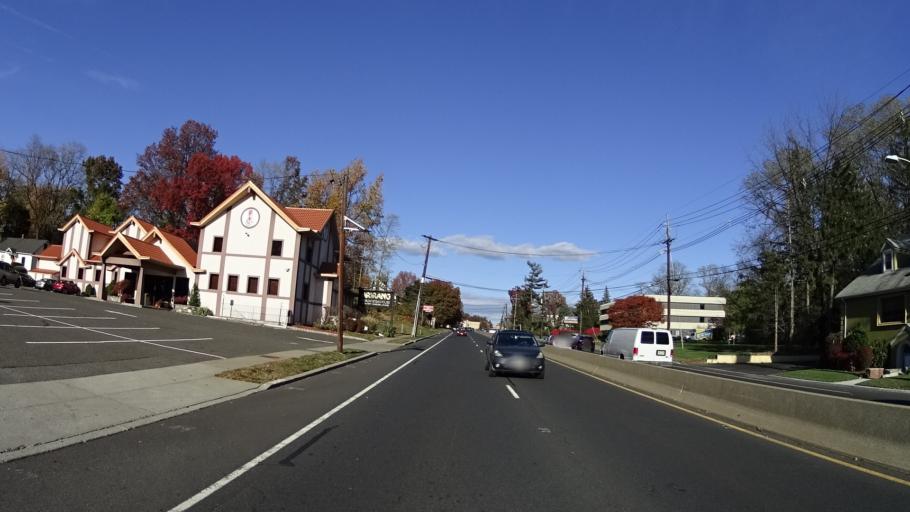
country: US
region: New Jersey
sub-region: Union County
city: Mountainside
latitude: 40.6765
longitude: -74.3476
